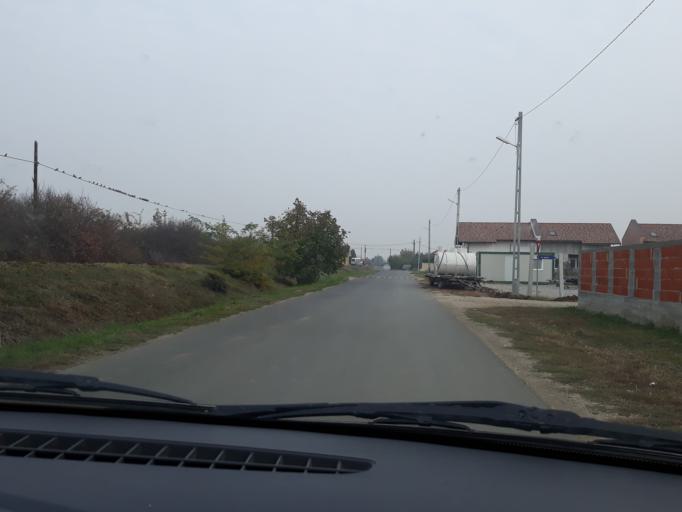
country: RO
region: Bihor
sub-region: Comuna Santandrei
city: Santandrei
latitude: 47.0627
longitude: 21.8566
